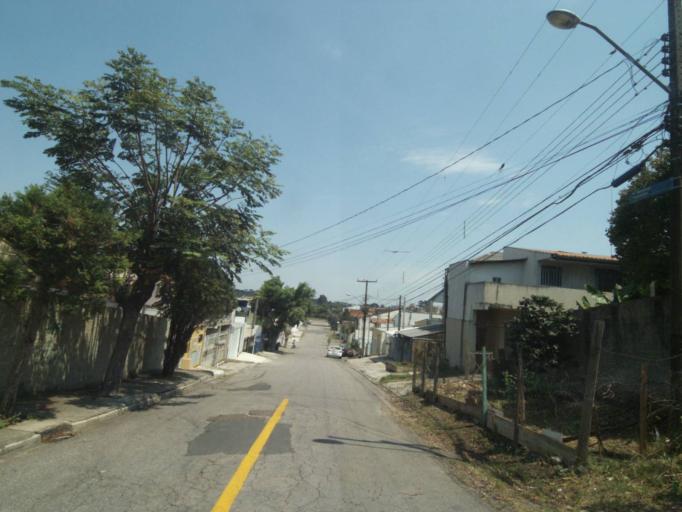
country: BR
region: Parana
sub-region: Sao Jose Dos Pinhais
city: Sao Jose dos Pinhais
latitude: -25.5207
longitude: -49.2659
